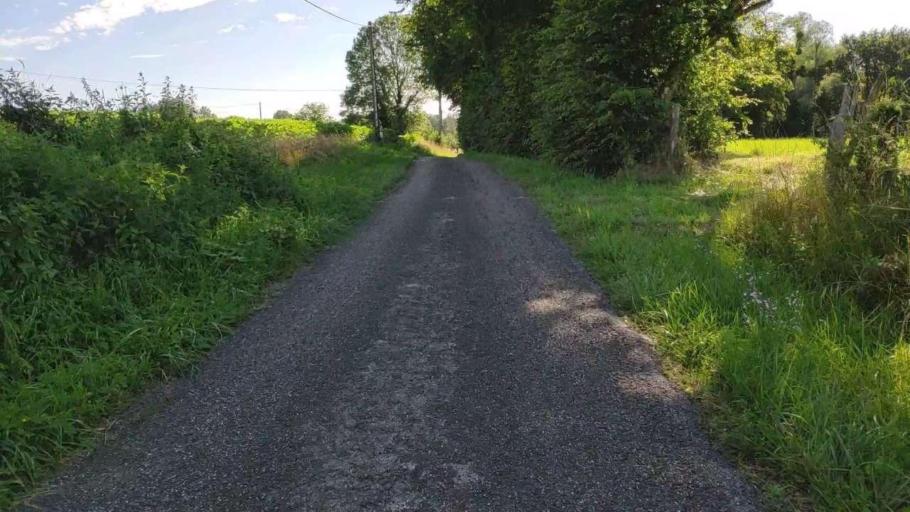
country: FR
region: Franche-Comte
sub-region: Departement du Jura
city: Bletterans
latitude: 46.8227
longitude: 5.5016
